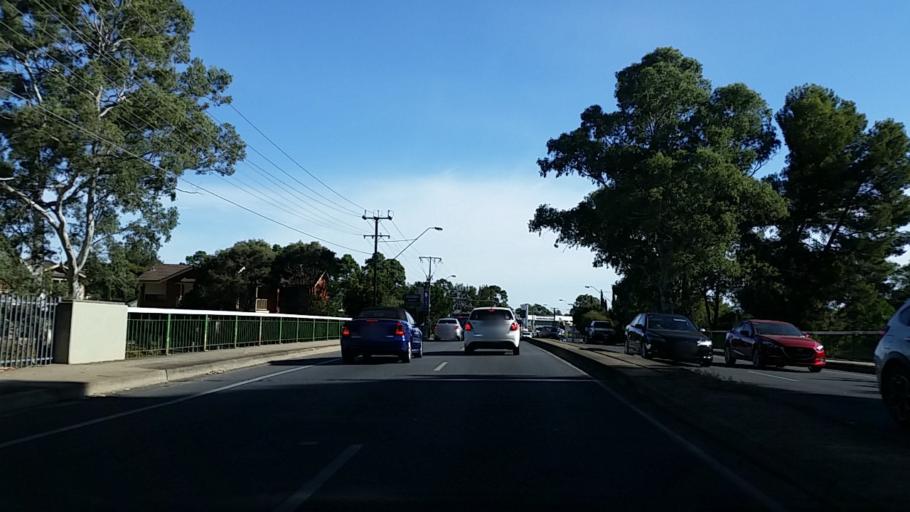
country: AU
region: South Australia
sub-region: Campbelltown
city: Paradise
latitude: -34.8678
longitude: 138.6768
